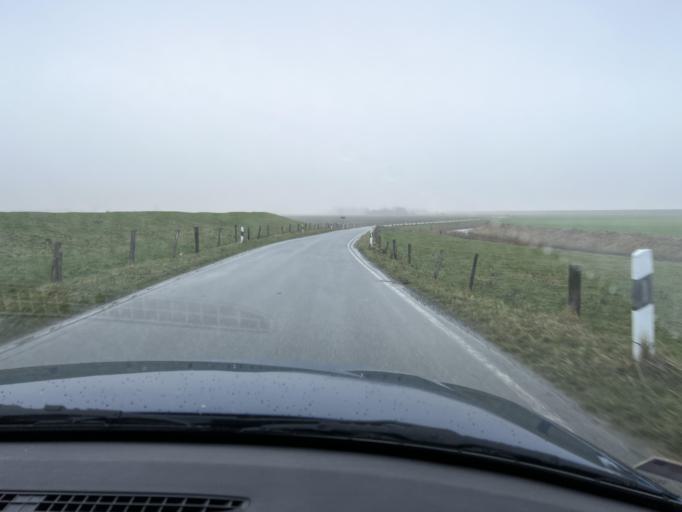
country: DE
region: Schleswig-Holstein
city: Schulp
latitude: 54.2640
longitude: 8.9293
